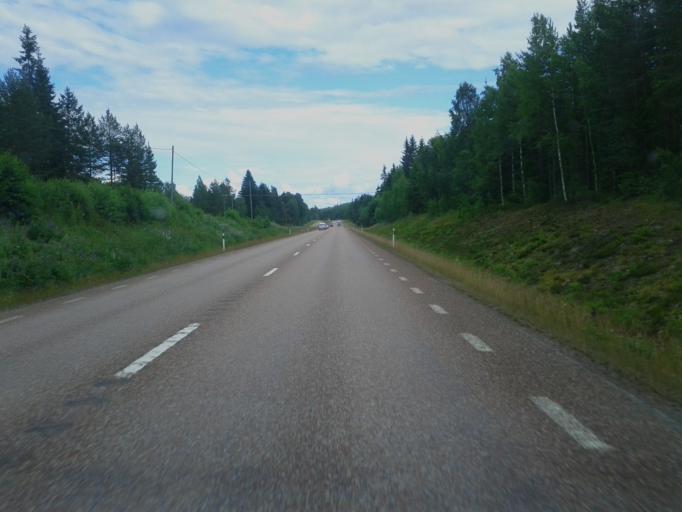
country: SE
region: Dalarna
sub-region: Faluns Kommun
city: Bjursas
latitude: 60.7432
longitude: 15.3942
